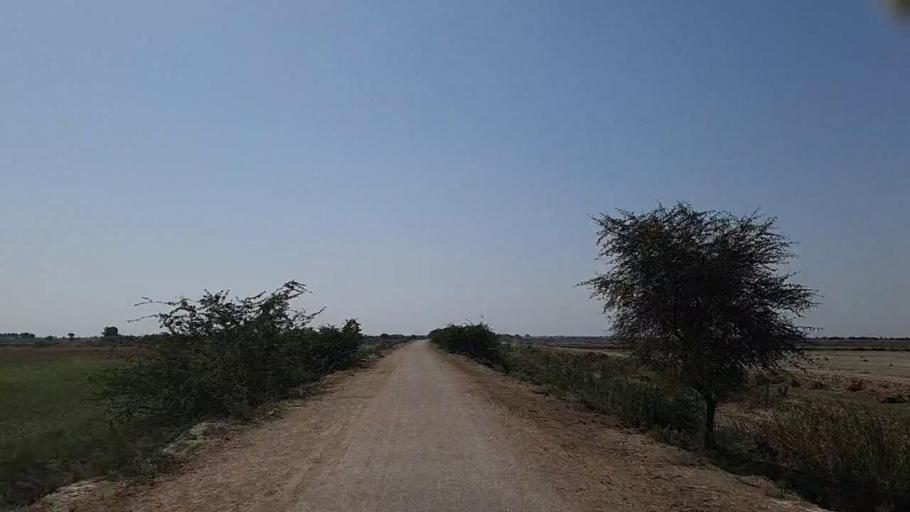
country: PK
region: Sindh
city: Mirpur Batoro
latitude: 24.6762
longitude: 68.3051
